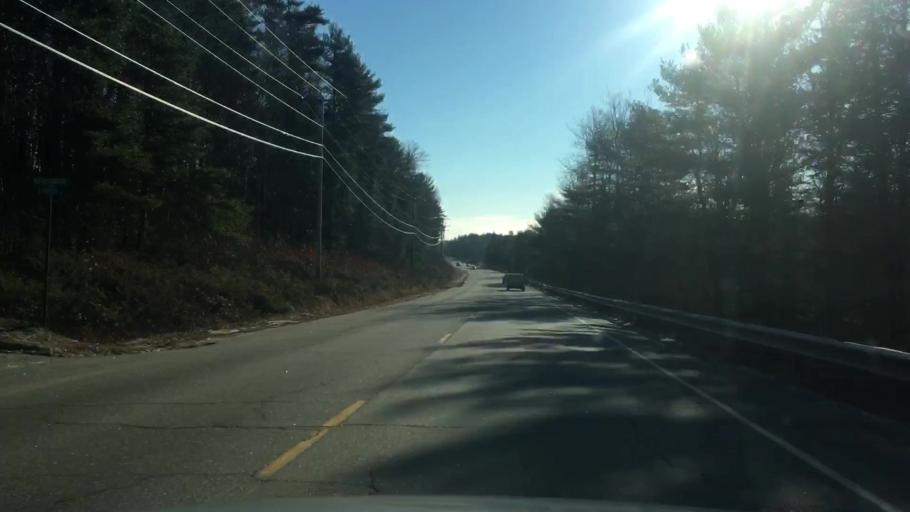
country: US
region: Maine
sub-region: Cumberland County
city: Brunswick
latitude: 43.8777
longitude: -69.9116
